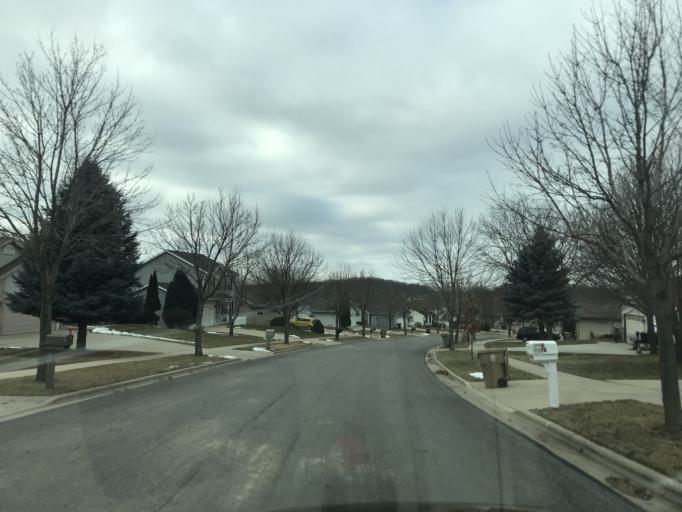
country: US
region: Wisconsin
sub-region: Dane County
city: Monona
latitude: 43.1082
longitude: -89.2938
